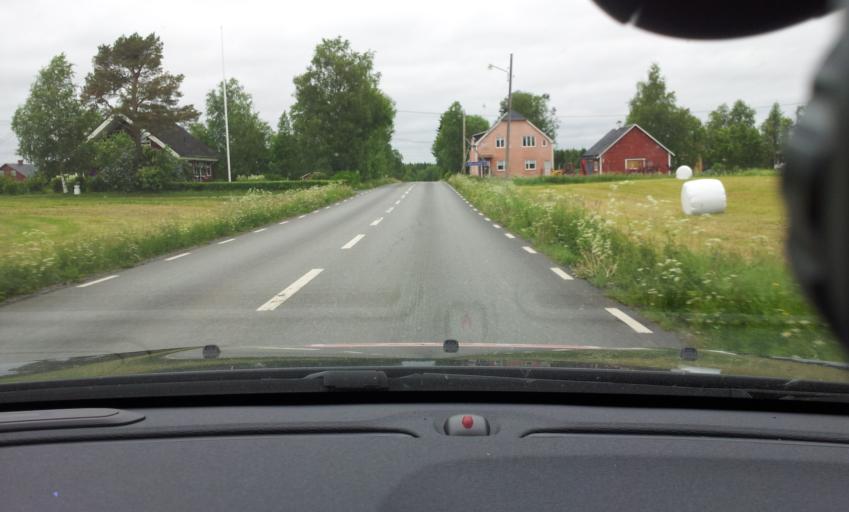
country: SE
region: Jaemtland
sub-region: Bergs Kommun
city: Hoverberg
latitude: 63.0695
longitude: 14.3176
